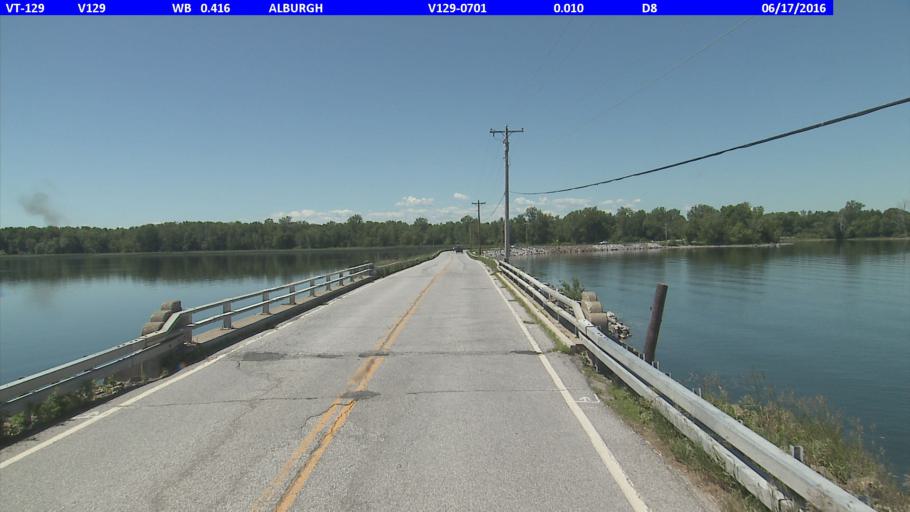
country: US
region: Vermont
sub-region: Grand Isle County
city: North Hero
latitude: 44.9035
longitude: -73.3158
